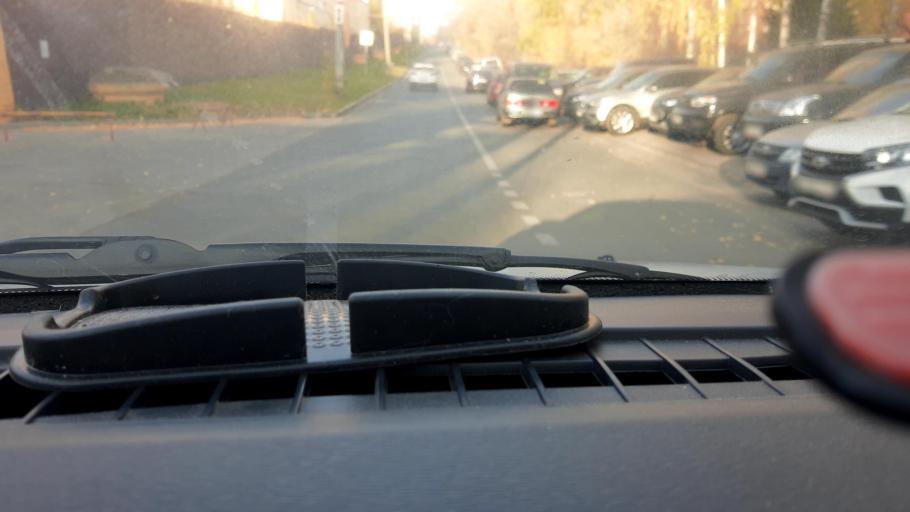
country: RU
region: Nizjnij Novgorod
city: Nizhniy Novgorod
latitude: 56.2505
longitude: 43.9753
